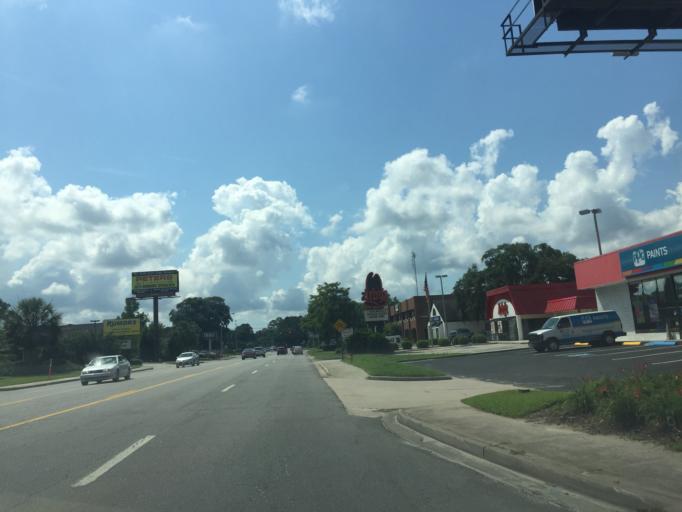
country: US
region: Georgia
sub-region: Chatham County
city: Isle of Hope
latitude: 32.0040
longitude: -81.1136
